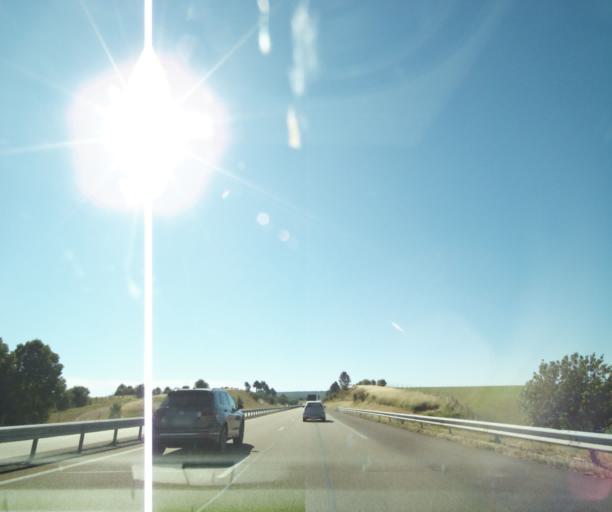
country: FR
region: Champagne-Ardenne
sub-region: Departement de la Haute-Marne
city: Rolampont
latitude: 47.9394
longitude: 5.1970
